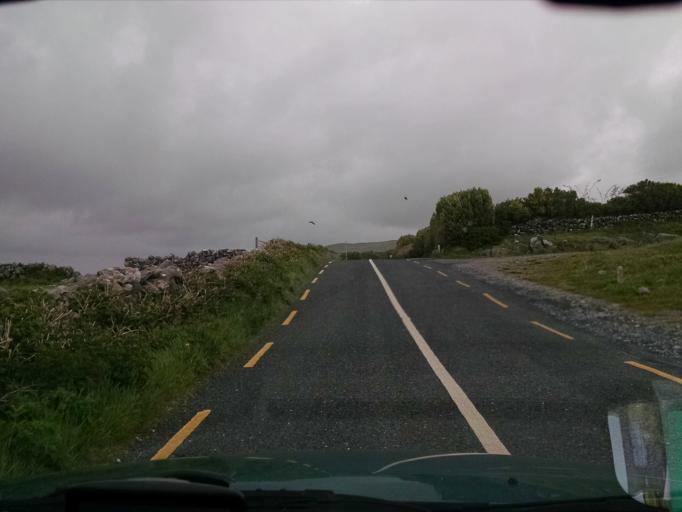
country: IE
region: Connaught
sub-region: County Galway
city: Bearna
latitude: 53.0932
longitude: -9.3074
